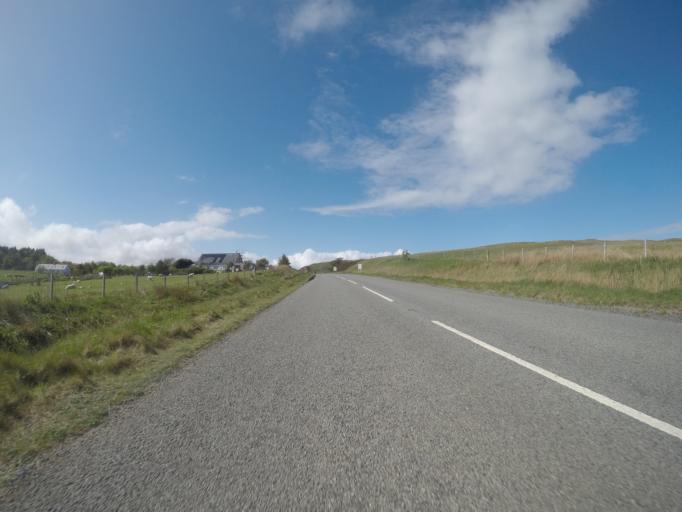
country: GB
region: Scotland
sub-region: Highland
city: Portree
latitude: 57.6109
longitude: -6.1757
